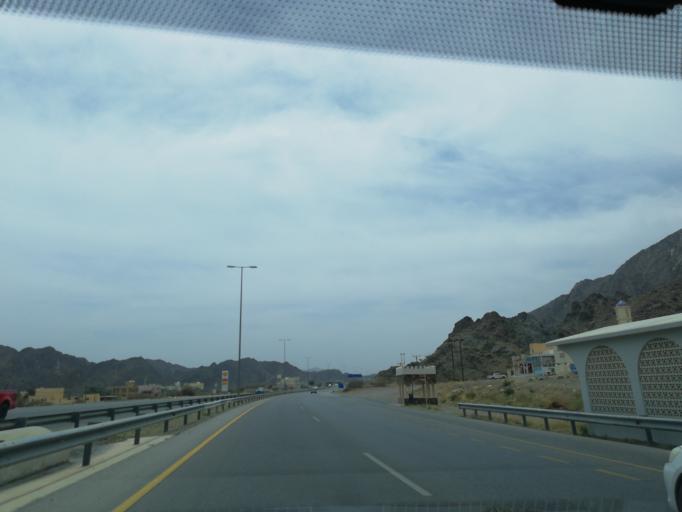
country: OM
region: Muhafazat ad Dakhiliyah
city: Izki
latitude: 23.1408
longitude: 57.8423
